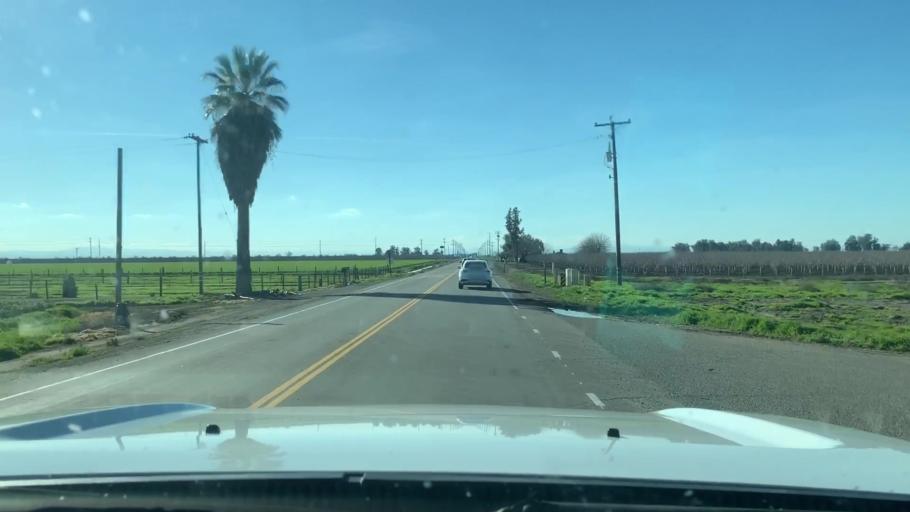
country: US
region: California
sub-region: Kings County
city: Home Garden
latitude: 36.2113
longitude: -119.6405
